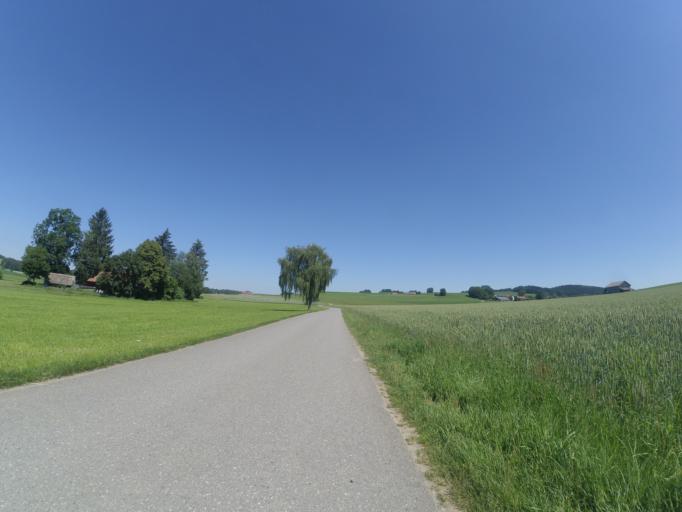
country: DE
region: Baden-Wuerttemberg
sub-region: Tuebingen Region
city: Bad Wurzach
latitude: 47.8819
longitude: 9.9176
